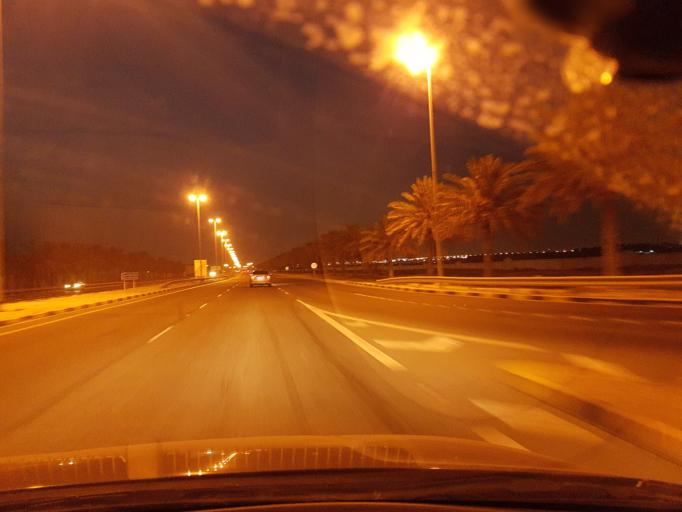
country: BH
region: Central Governorate
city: Dar Kulayb
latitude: 26.0384
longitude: 50.5000
